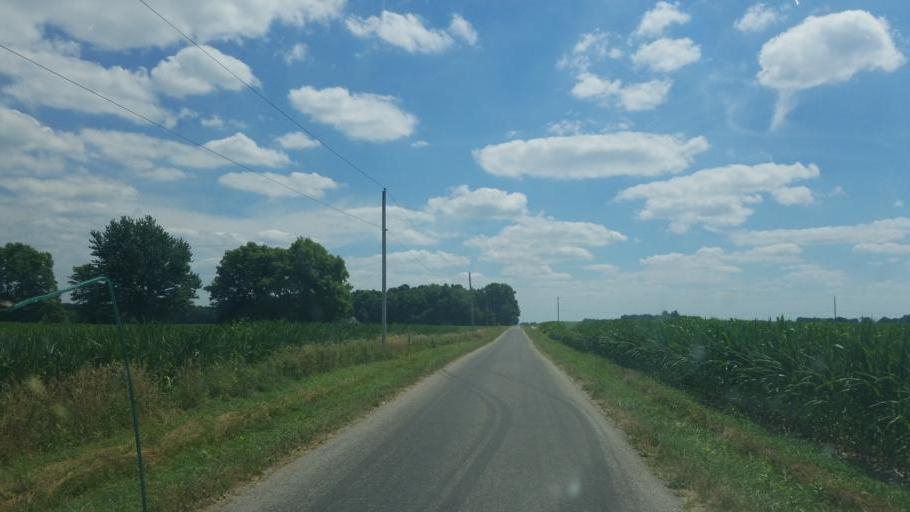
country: US
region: Ohio
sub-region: Defiance County
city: Hicksville
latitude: 41.3561
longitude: -84.6902
